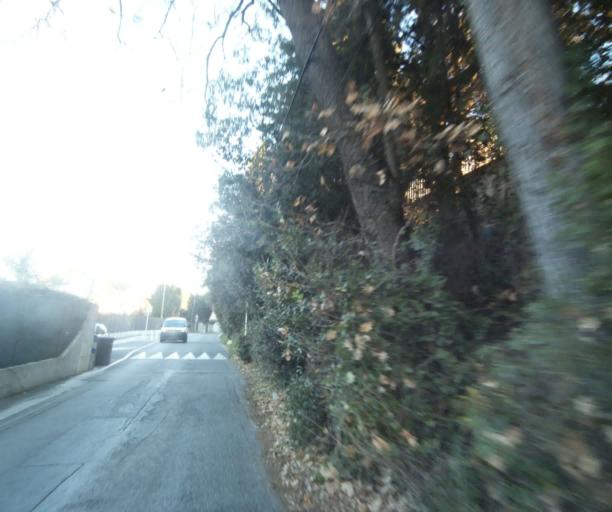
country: FR
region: Provence-Alpes-Cote d'Azur
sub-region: Departement des Alpes-Maritimes
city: Vallauris
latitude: 43.5816
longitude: 7.0817
